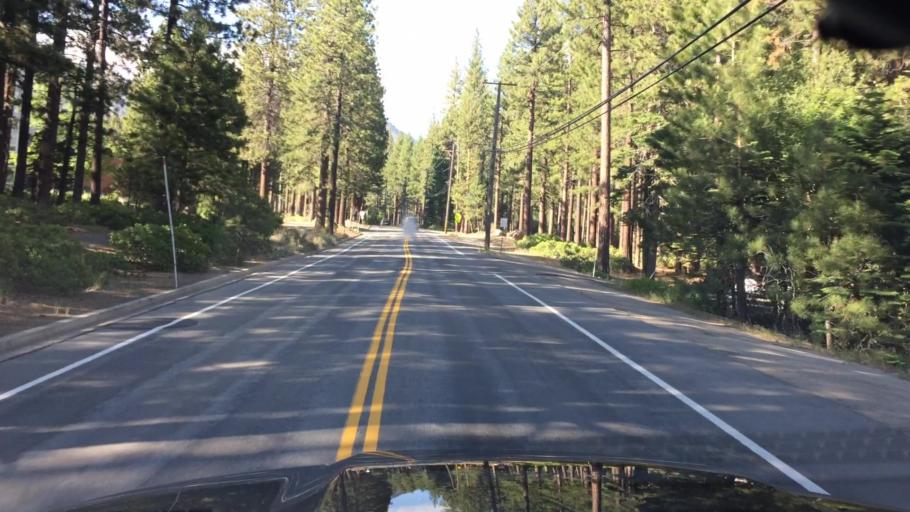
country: US
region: Nevada
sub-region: Washoe County
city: Incline Village
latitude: 39.2534
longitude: -119.9515
